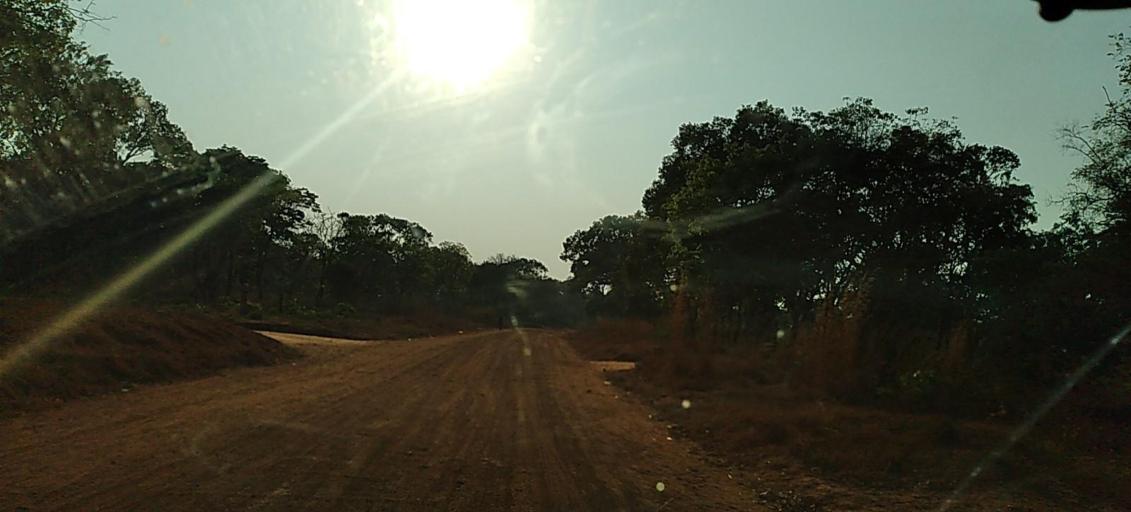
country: ZM
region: North-Western
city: Kasempa
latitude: -13.4719
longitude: 25.8699
